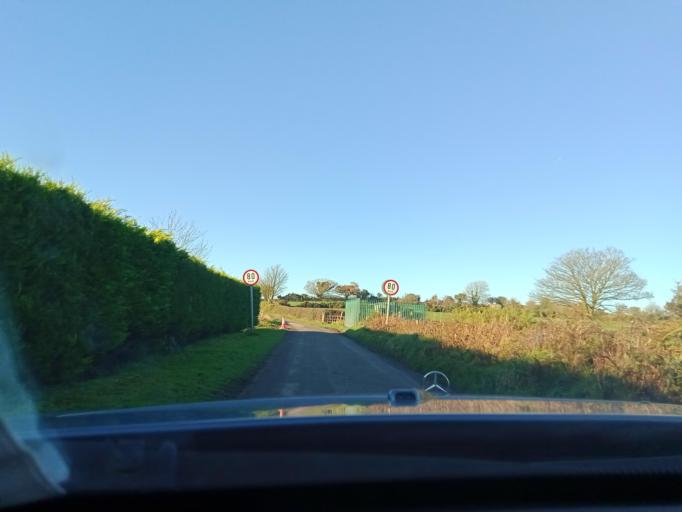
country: IE
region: Leinster
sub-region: Kilkenny
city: Callan
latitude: 52.4604
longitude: -7.4015
